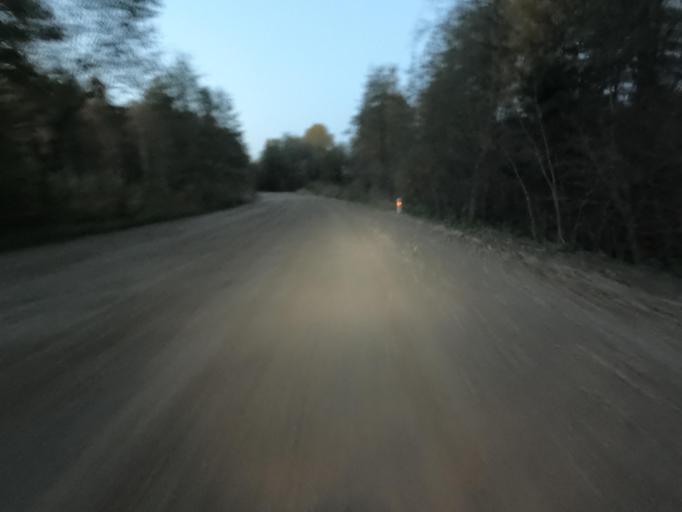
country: RU
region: Leningrad
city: Lyuban'
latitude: 59.1885
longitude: 31.2504
